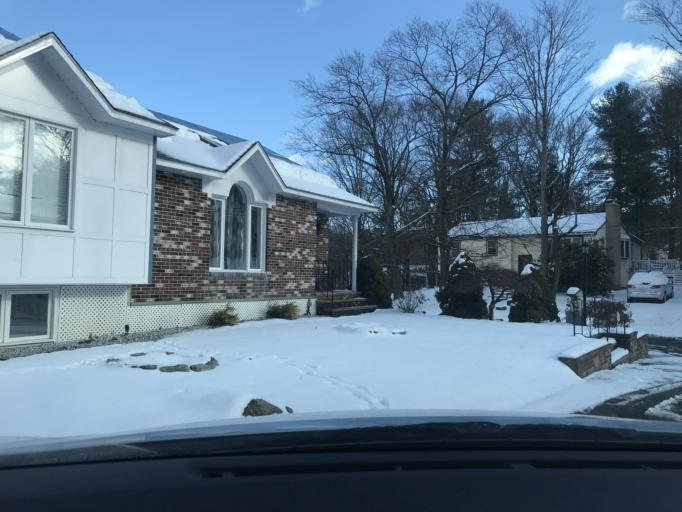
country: US
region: Massachusetts
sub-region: Essex County
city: Saugus
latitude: 42.4891
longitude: -71.0137
